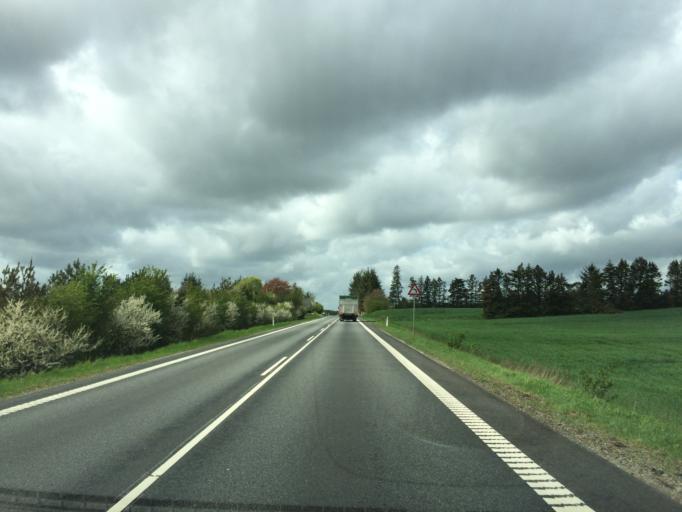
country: DK
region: Central Jutland
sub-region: Viborg Kommune
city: Stoholm
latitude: 56.4387
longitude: 9.2118
